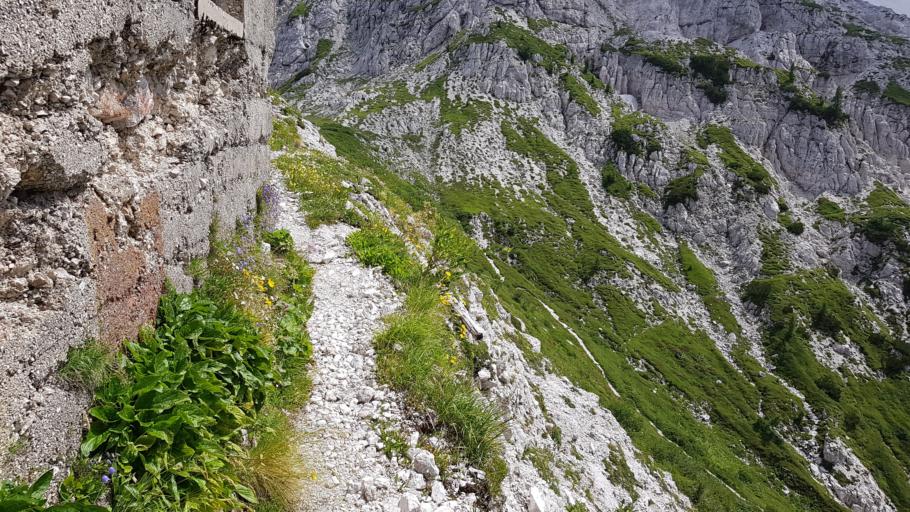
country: SI
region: Bovec
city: Bovec
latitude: 46.3842
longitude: 13.5159
